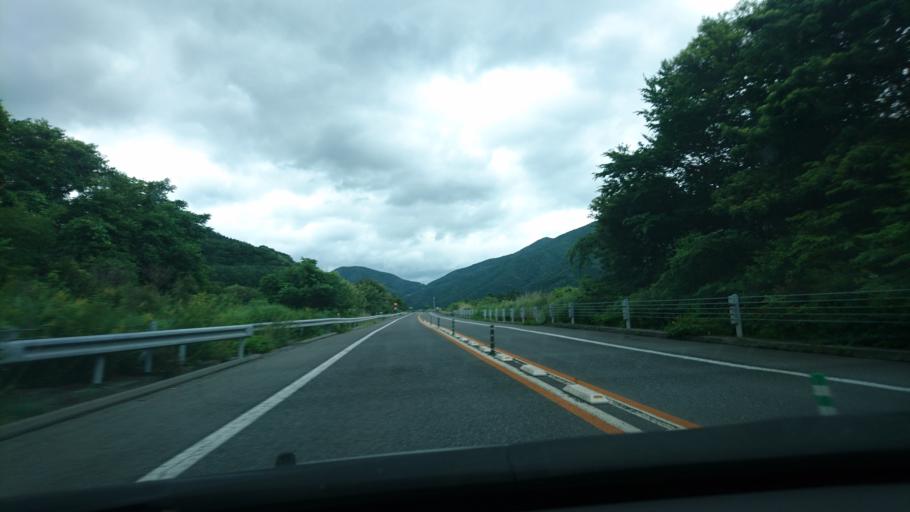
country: JP
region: Iwate
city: Ofunato
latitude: 39.1252
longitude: 141.7314
